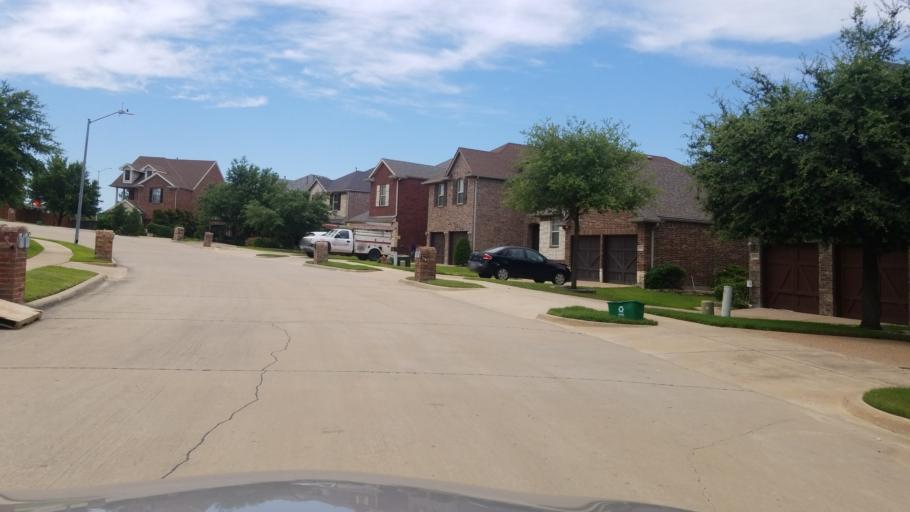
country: US
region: Texas
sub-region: Dallas County
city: Grand Prairie
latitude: 32.6775
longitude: -96.9960
